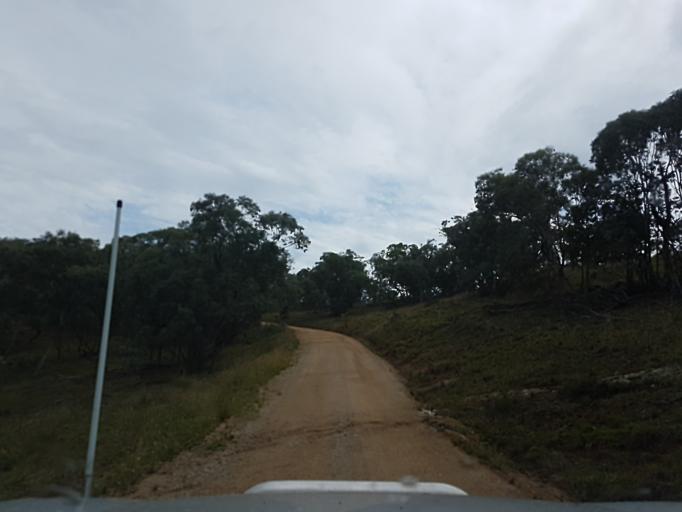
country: AU
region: New South Wales
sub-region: Snowy River
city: Jindabyne
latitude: -36.9427
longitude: 148.3461
